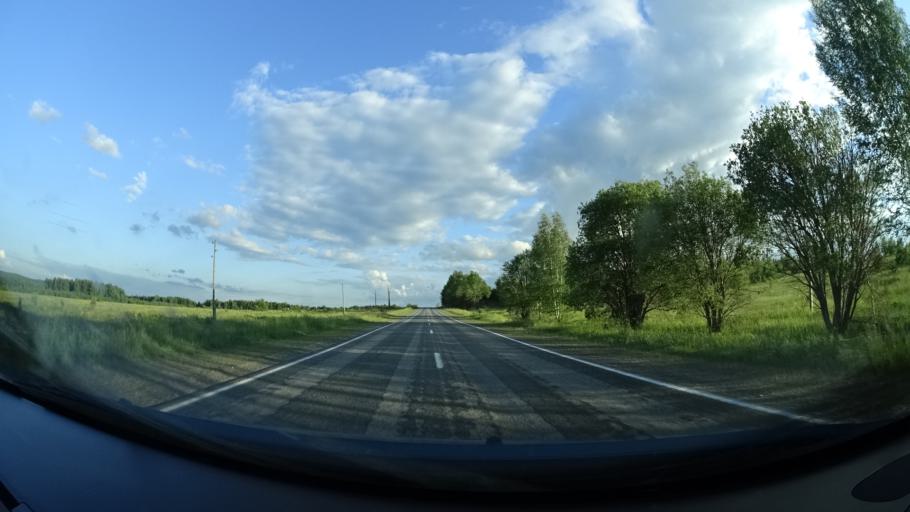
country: RU
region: Perm
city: Osa
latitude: 57.1318
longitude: 55.5260
